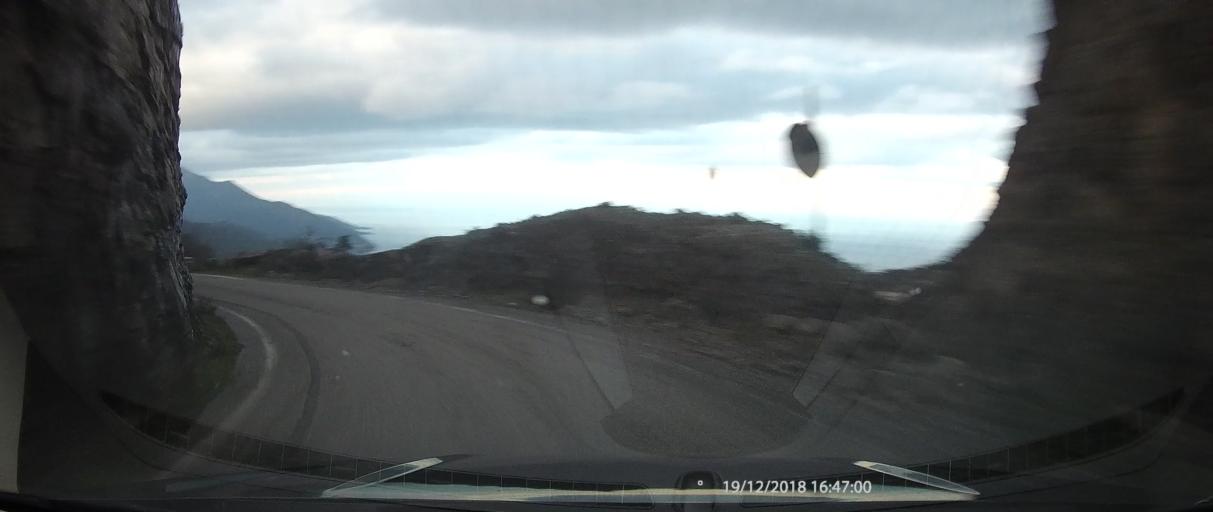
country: GR
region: Peloponnese
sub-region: Nomos Lakonias
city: Sykea
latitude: 36.9257
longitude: 23.0068
